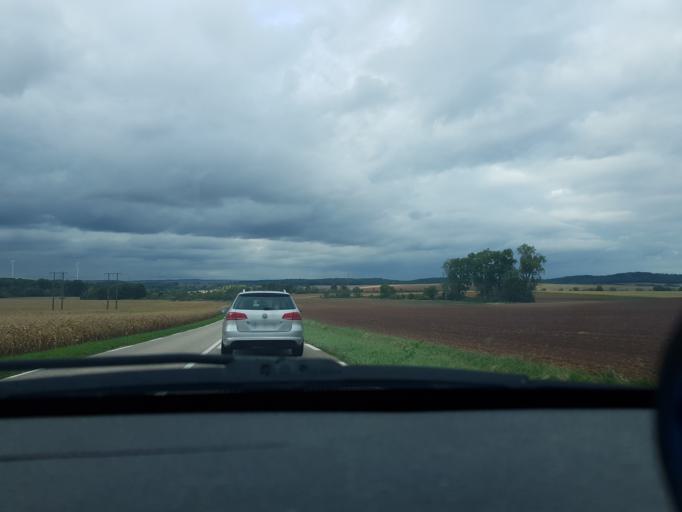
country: FR
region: Lorraine
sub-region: Departement de la Moselle
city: Morhange
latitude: 48.9451
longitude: 6.6108
